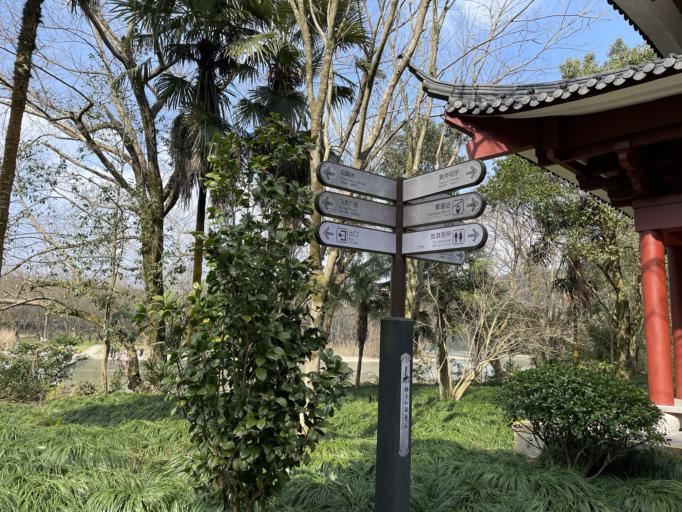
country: CN
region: Zhejiang Sheng
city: Shuhong
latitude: 28.6917
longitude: 120.1382
